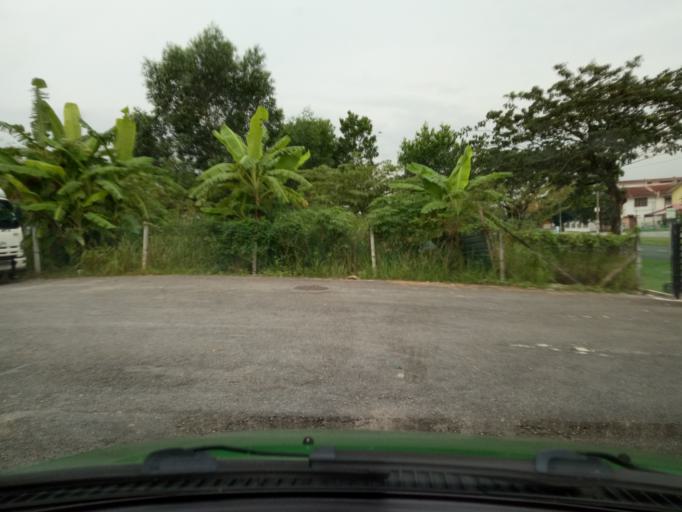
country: MY
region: Selangor
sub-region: Hulu Langat
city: Semenyih
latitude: 2.9314
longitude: 101.8638
